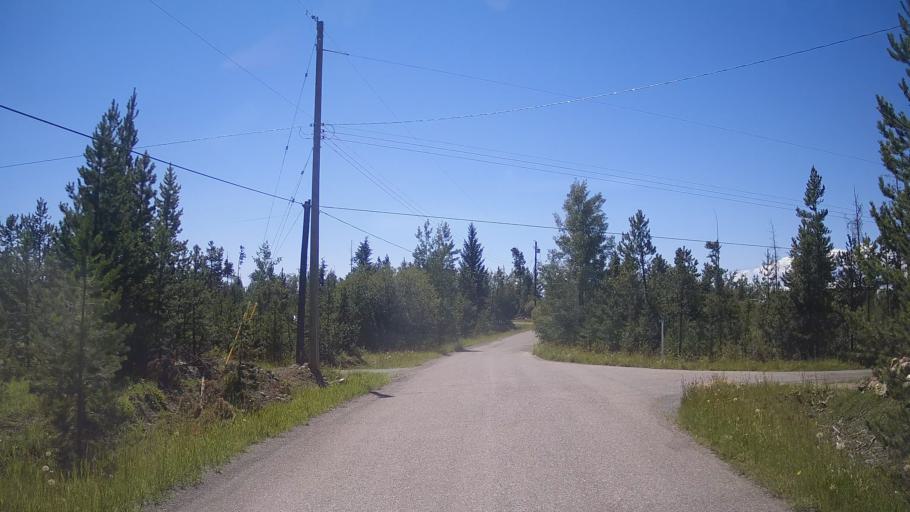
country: CA
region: British Columbia
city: Cache Creek
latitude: 51.3157
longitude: -121.3933
